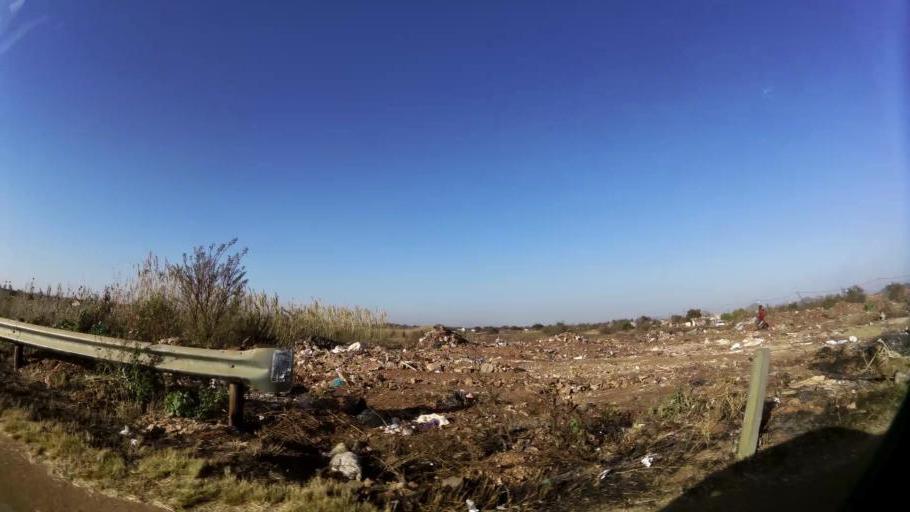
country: ZA
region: Gauteng
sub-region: City of Tshwane Metropolitan Municipality
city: Mabopane
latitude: -25.5922
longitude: 28.1090
